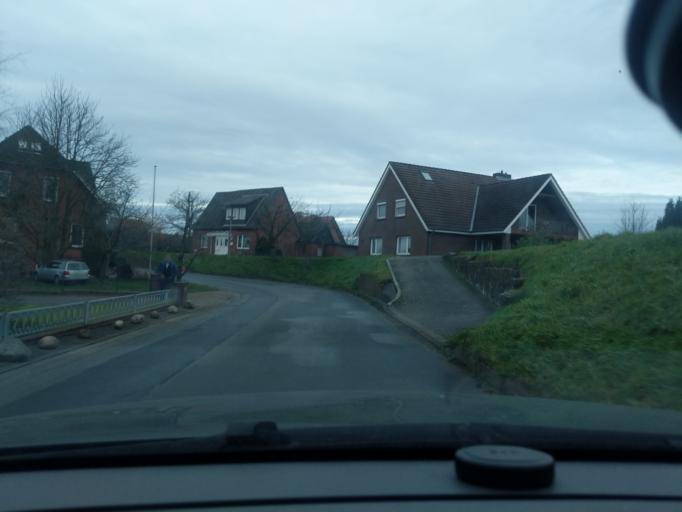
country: DE
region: Lower Saxony
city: Mittelnkirchen
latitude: 53.5348
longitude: 9.6129
